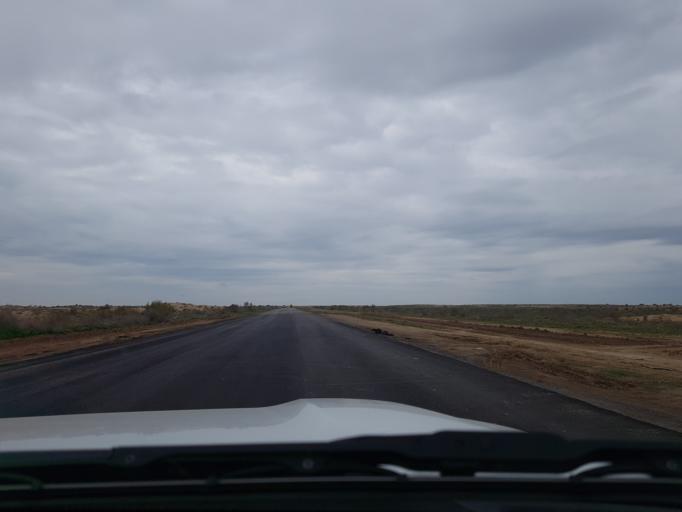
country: TM
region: Mary
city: Bayramaly
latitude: 37.6919
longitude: 62.4120
